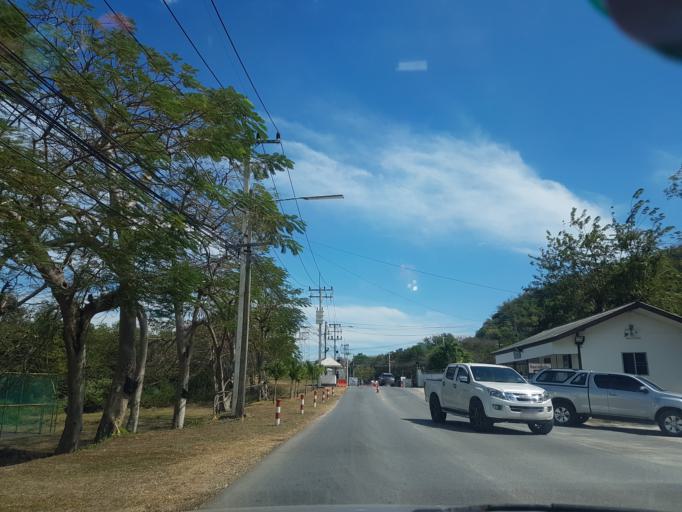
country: TH
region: Chon Buri
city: Sattahip
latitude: 12.6379
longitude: 100.9429
